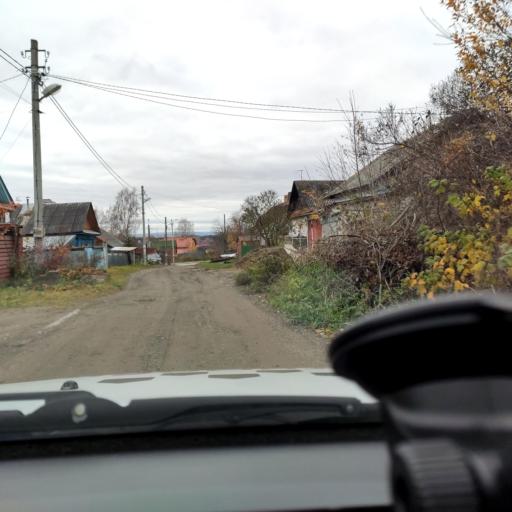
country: RU
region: Perm
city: Kondratovo
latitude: 58.0462
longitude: 56.1173
